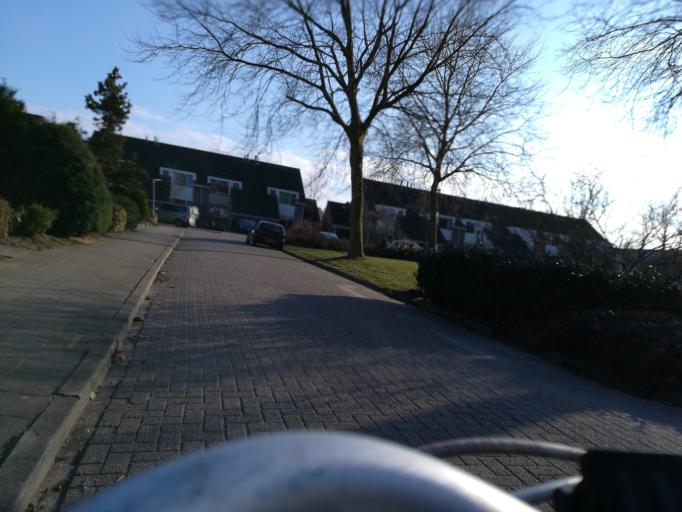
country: NL
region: Gelderland
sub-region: Gemeente Epe
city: Epe
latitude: 52.3416
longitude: 5.9763
